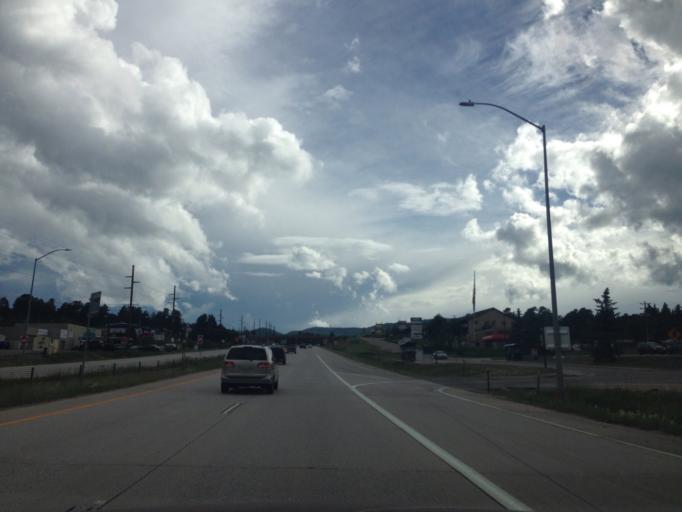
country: US
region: Colorado
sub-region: Jefferson County
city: Evergreen
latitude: 39.5414
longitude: -105.2969
